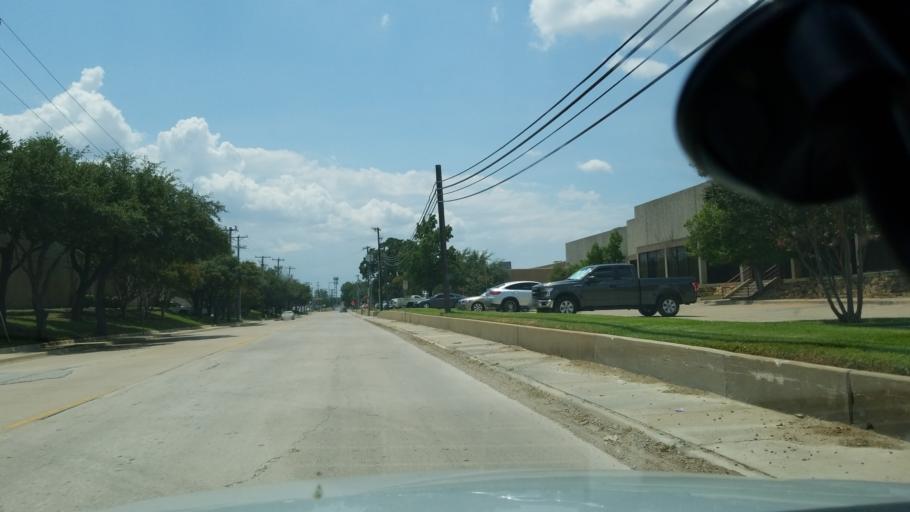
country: US
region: Texas
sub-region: Dallas County
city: Farmers Branch
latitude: 32.8702
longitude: -96.9079
